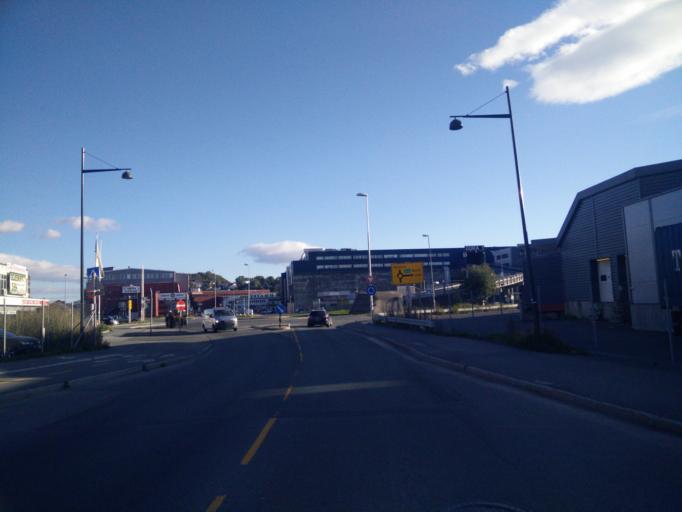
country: NO
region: Sor-Trondelag
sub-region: Trondheim
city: Trondheim
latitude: 63.4379
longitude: 10.4175
